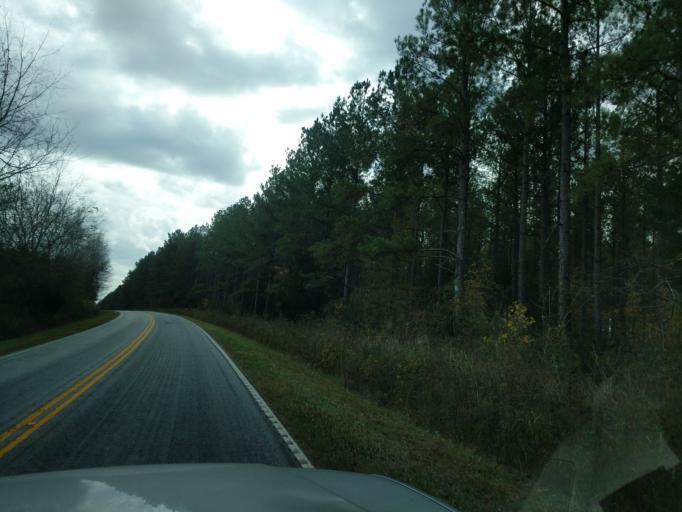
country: US
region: South Carolina
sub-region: Laurens County
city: Clinton
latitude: 34.4194
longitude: -81.8689
